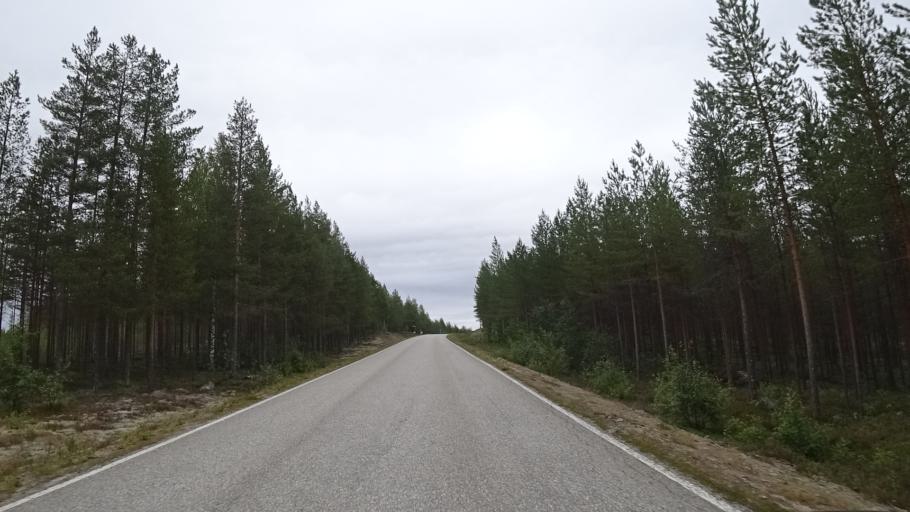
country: FI
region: North Karelia
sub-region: Pielisen Karjala
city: Lieksa
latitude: 63.3812
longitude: 30.3206
